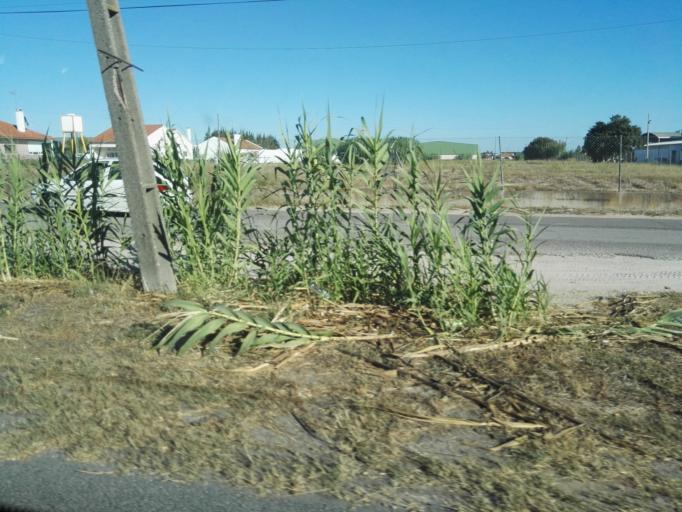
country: PT
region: Santarem
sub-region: Benavente
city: Benavente
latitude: 38.9557
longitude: -8.8240
